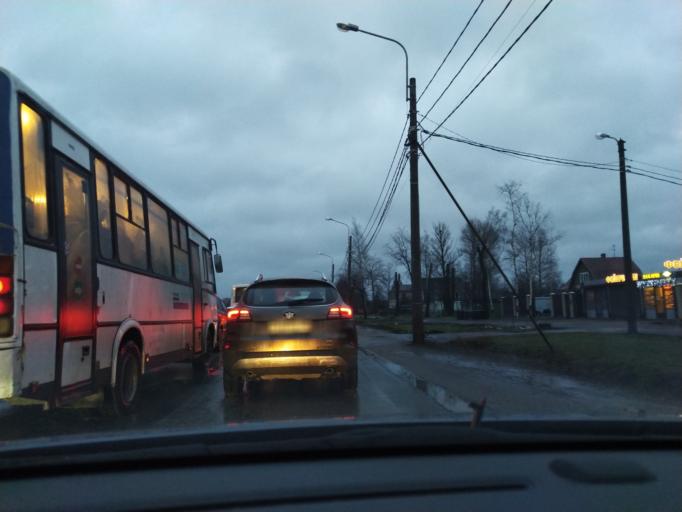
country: RU
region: St.-Petersburg
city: Uritsk
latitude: 59.8139
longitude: 30.1734
